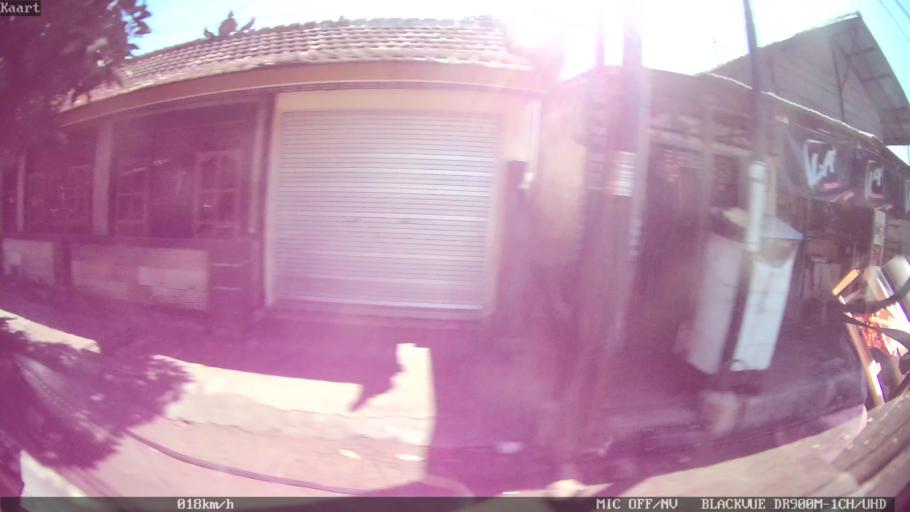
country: ID
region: Bali
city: Banjar Sidayu
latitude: -8.1028
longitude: 115.1202
